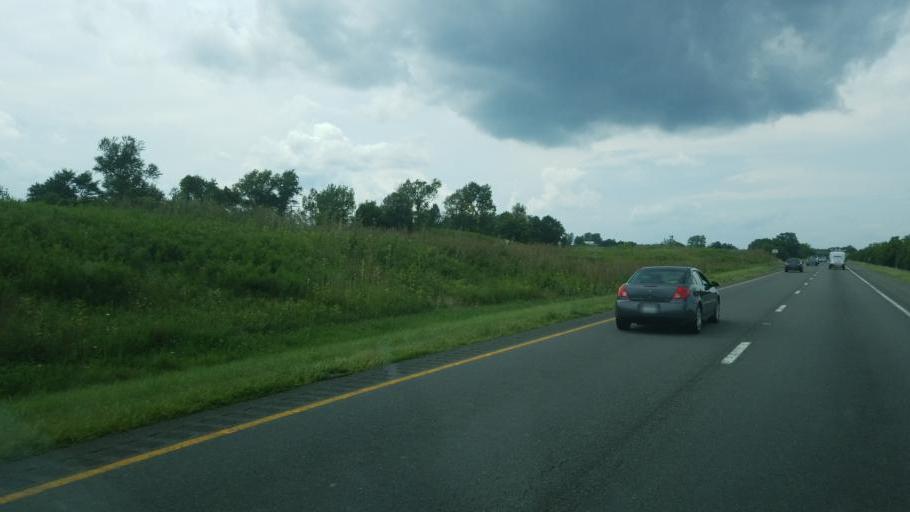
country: US
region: Virginia
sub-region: Warren County
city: Apple Mountain Lake
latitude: 38.9423
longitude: -78.1368
